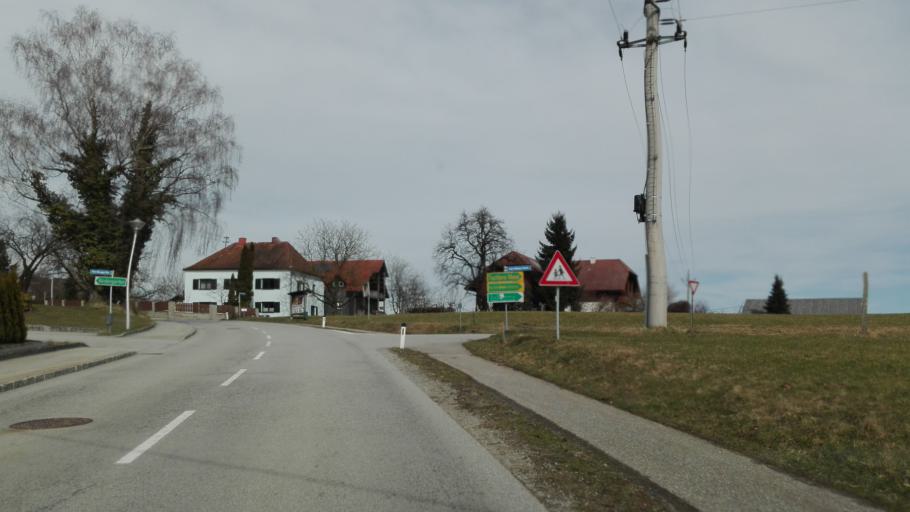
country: DE
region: Bavaria
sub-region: Lower Bavaria
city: Passau
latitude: 48.5170
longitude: 13.4946
